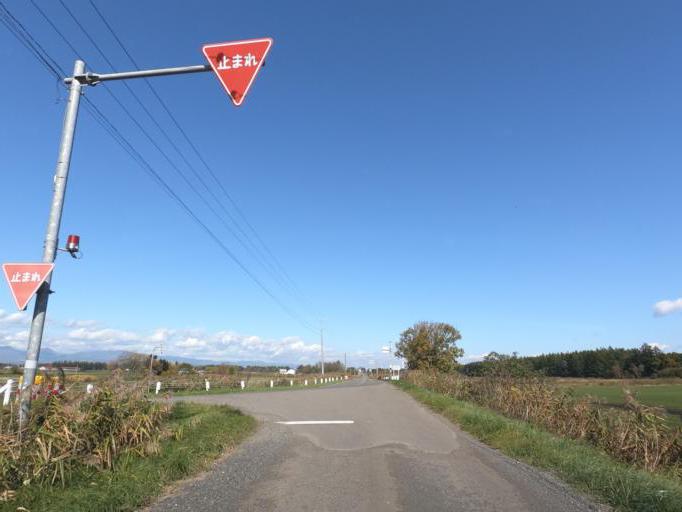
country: JP
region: Hokkaido
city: Otofuke
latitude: 43.0833
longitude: 143.2614
